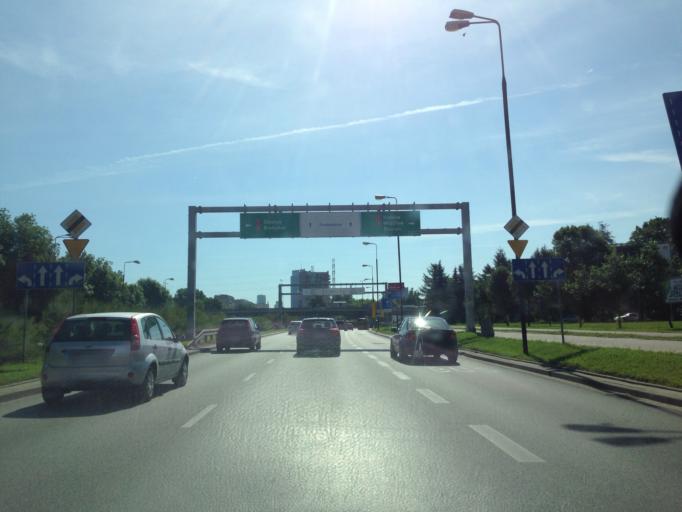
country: PL
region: Masovian Voivodeship
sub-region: Warszawa
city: Wola
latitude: 52.2381
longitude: 20.9528
